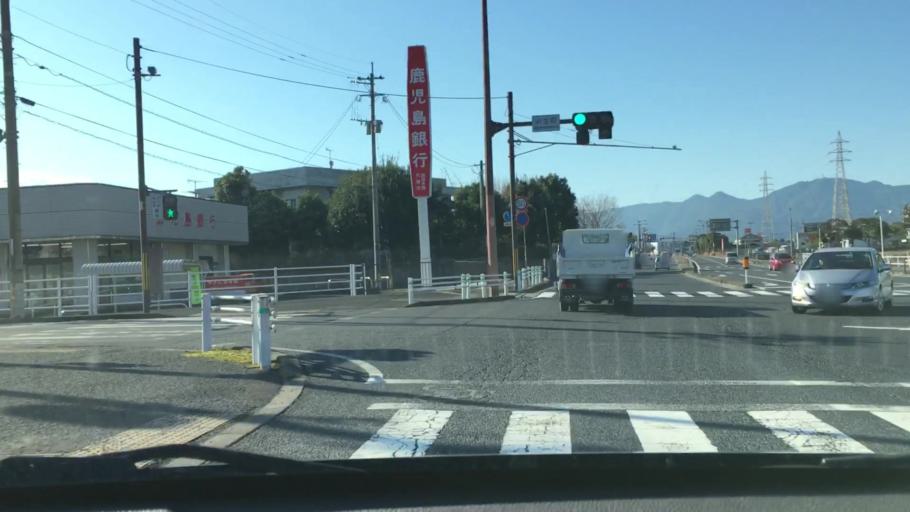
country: JP
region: Kagoshima
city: Kajiki
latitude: 31.7391
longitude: 130.6514
